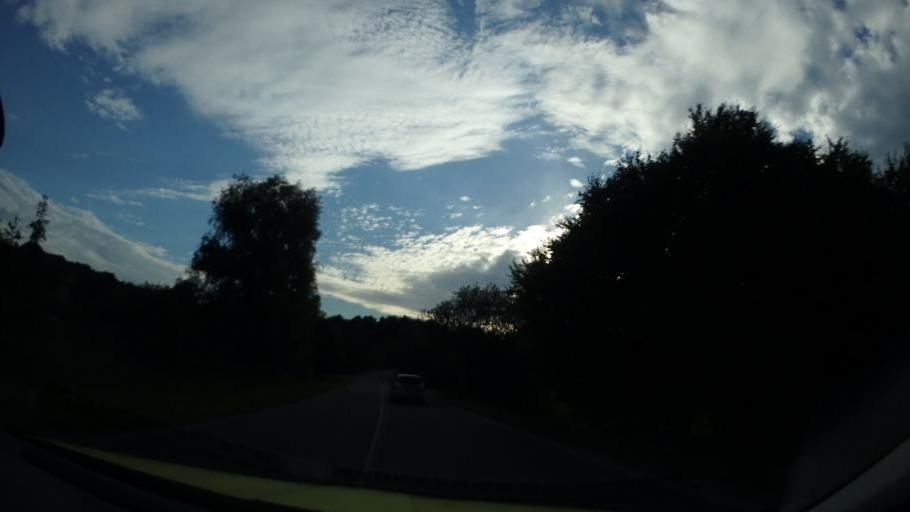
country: CZ
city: Stramberk
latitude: 49.5946
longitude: 18.1007
